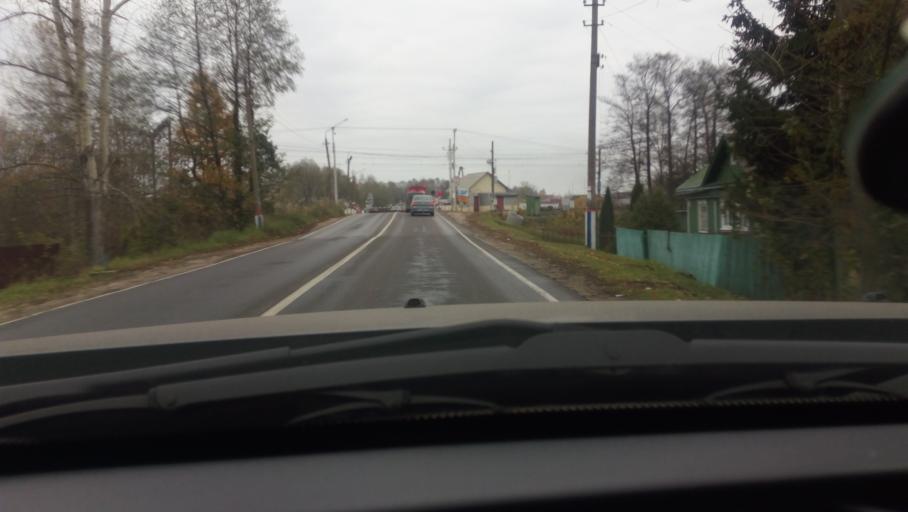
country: RU
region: Moskovskaya
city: Likino-Dulevo
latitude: 55.7005
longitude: 38.9439
